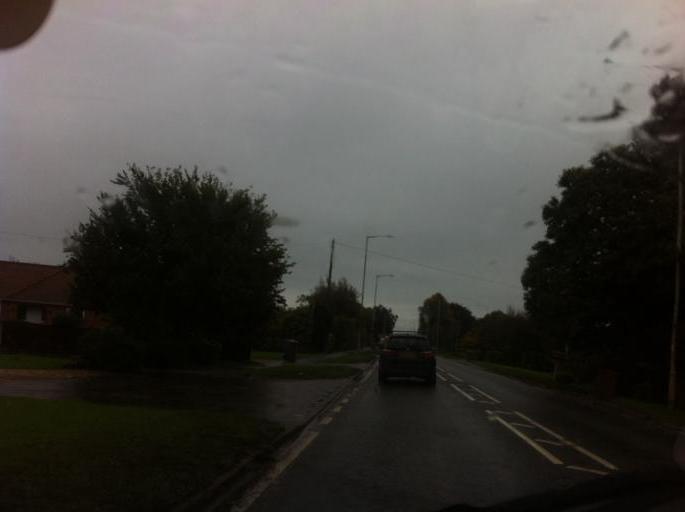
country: GB
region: England
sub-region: Lincolnshire
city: Boston
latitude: 52.9882
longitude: -0.0026
